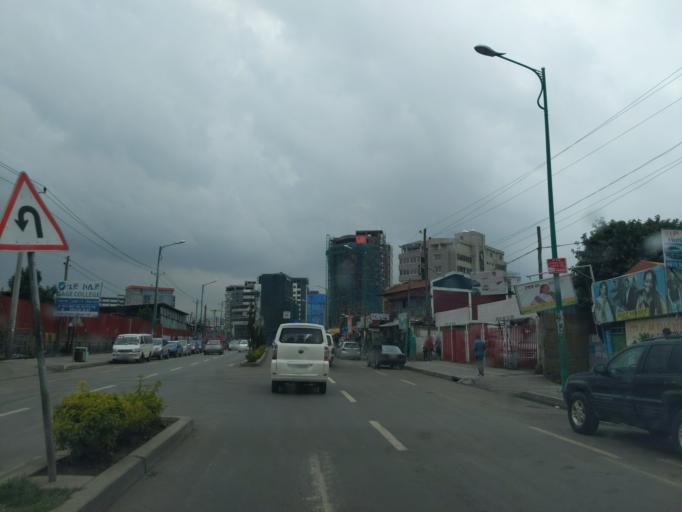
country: ET
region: Adis Abeba
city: Addis Ababa
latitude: 8.9983
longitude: 38.7669
